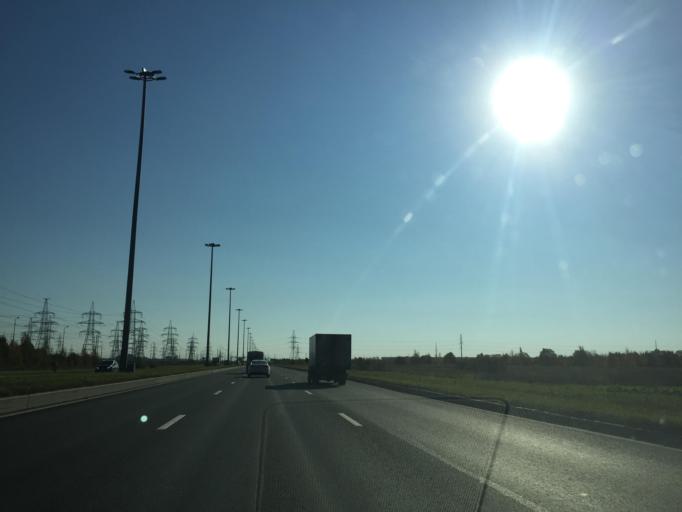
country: RU
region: St.-Petersburg
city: Petro-Slavyanka
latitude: 59.7575
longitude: 30.5164
